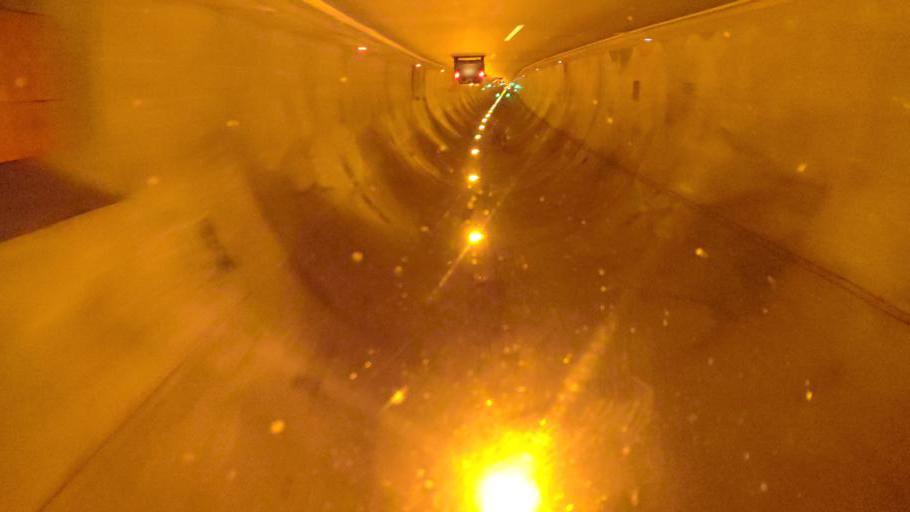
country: GR
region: Epirus
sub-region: Nomos Ioanninon
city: Katsikas
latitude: 39.6954
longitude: 20.9683
